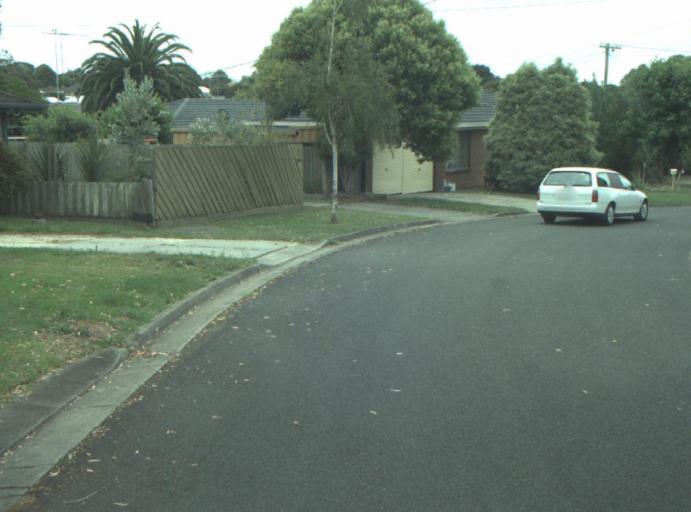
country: AU
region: Victoria
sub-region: Greater Geelong
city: Breakwater
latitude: -38.1869
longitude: 144.3410
